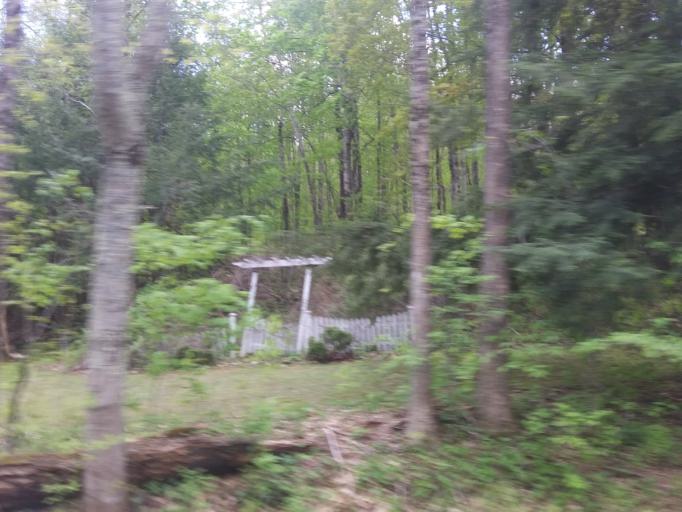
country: US
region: Massachusetts
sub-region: Franklin County
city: Buckland
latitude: 42.5655
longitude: -72.8052
